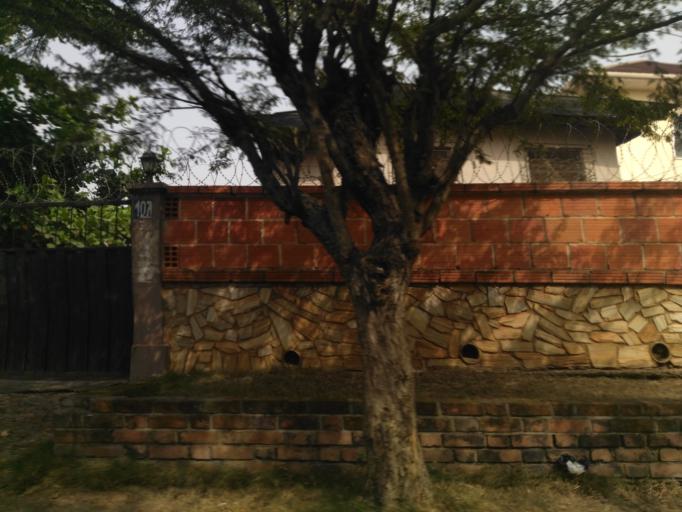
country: GH
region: Ashanti
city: Kumasi
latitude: 6.6764
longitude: -1.6061
